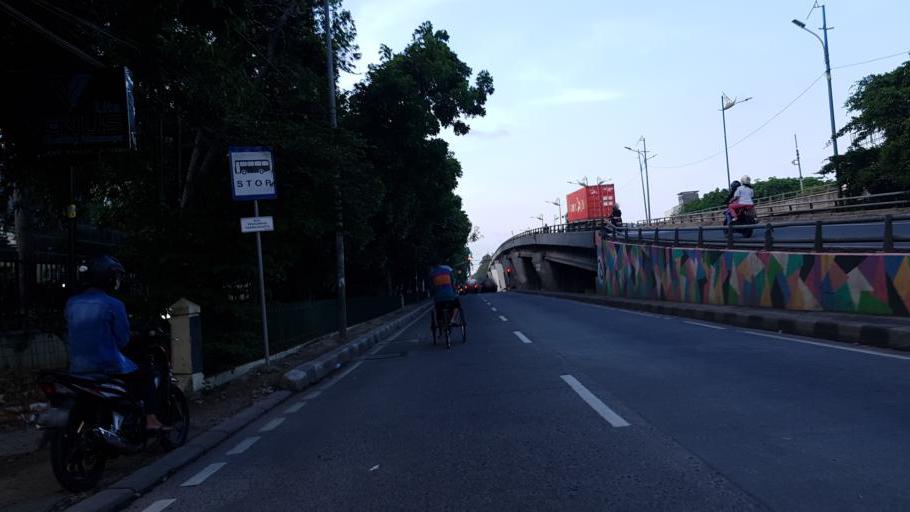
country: ID
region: Jakarta Raya
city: Jakarta
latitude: -6.1386
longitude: 106.7929
